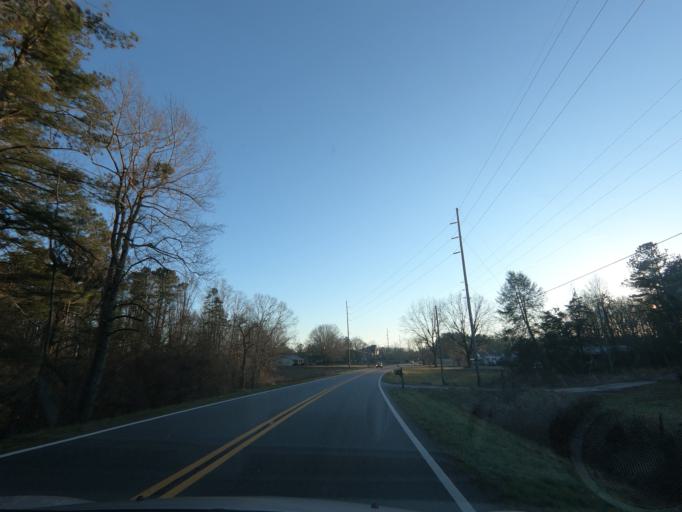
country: US
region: Georgia
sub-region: Forsyth County
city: Cumming
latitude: 34.3137
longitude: -84.1439
